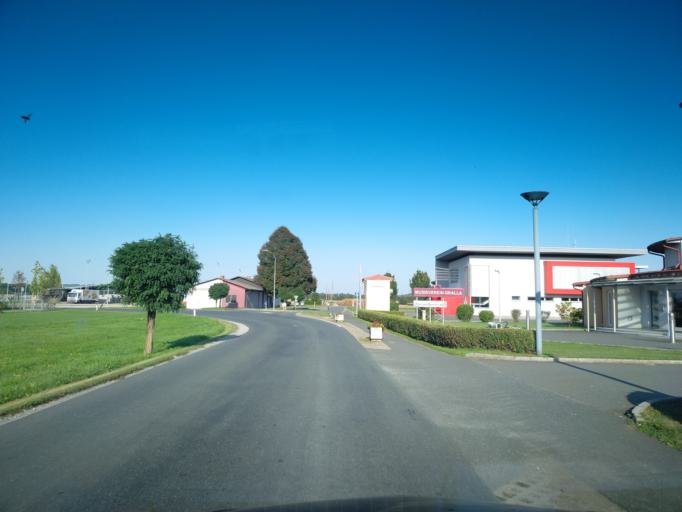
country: AT
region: Styria
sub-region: Politischer Bezirk Leibnitz
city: Kaindorf an der Sulm
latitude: 46.8153
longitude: 15.5562
